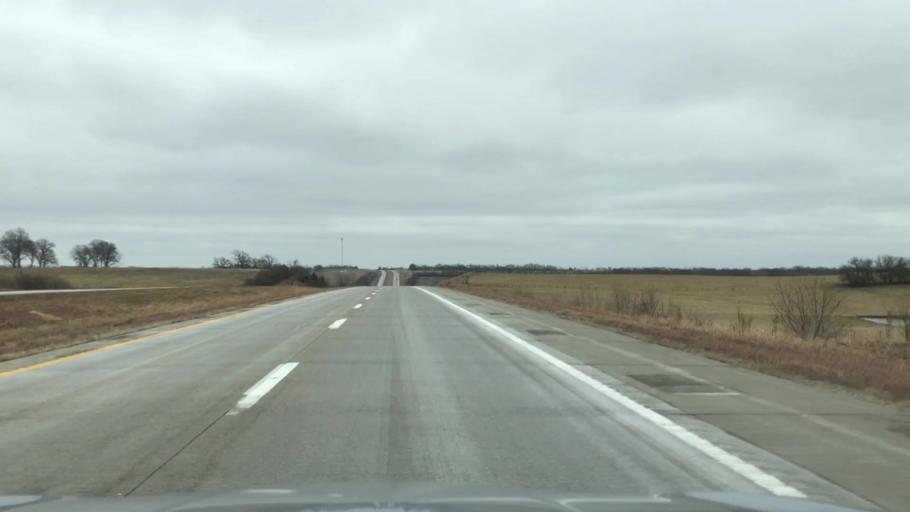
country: US
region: Missouri
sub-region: Caldwell County
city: Hamilton
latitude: 39.7349
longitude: -93.7916
